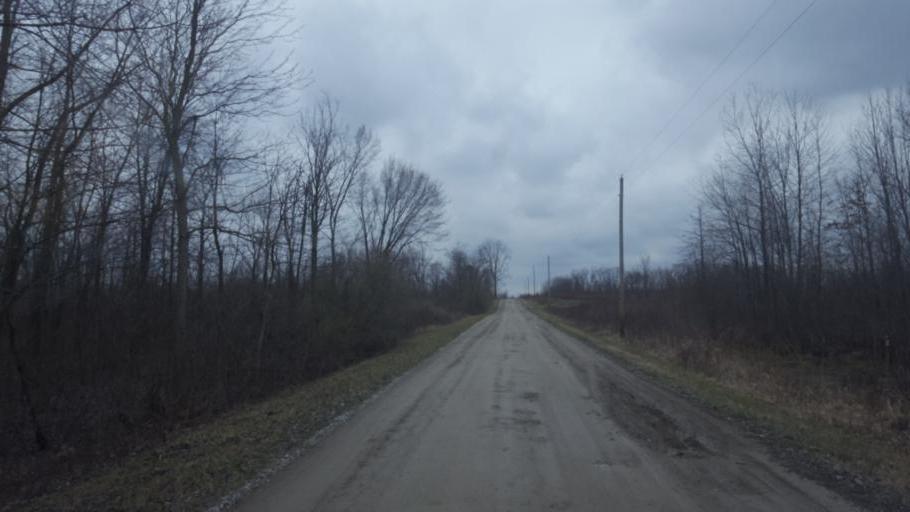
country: US
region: Ohio
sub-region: Delaware County
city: Delaware
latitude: 40.3662
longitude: -83.0374
